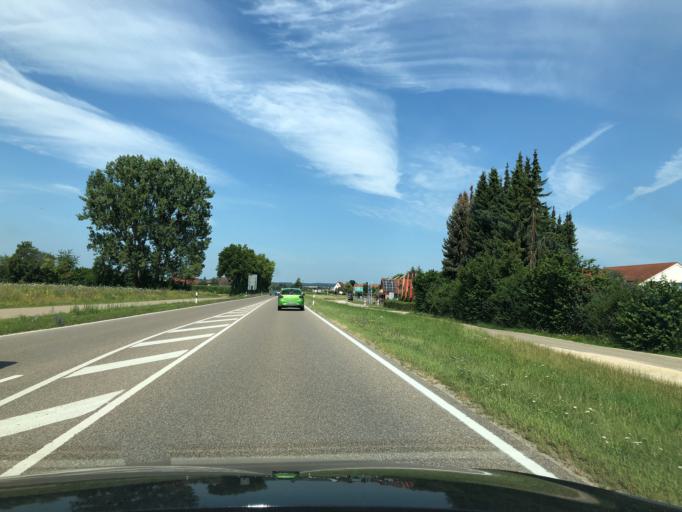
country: DE
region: Bavaria
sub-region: Upper Bavaria
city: Neuburg an der Donau
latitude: 48.7185
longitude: 11.2234
